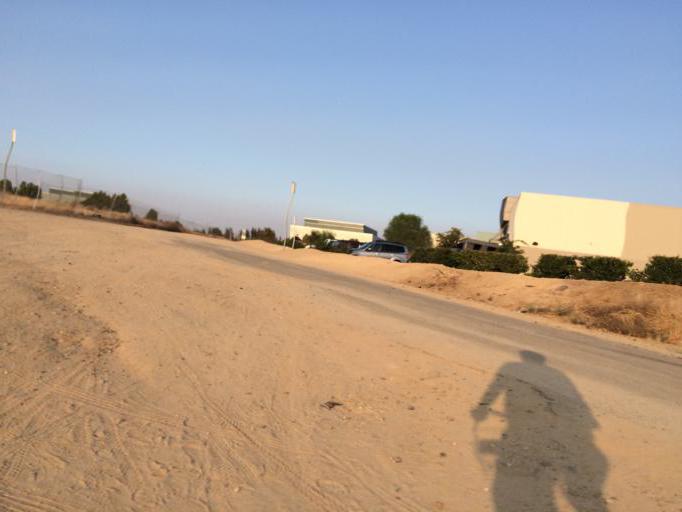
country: US
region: California
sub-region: Fresno County
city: Clovis
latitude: 36.8517
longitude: -119.8079
